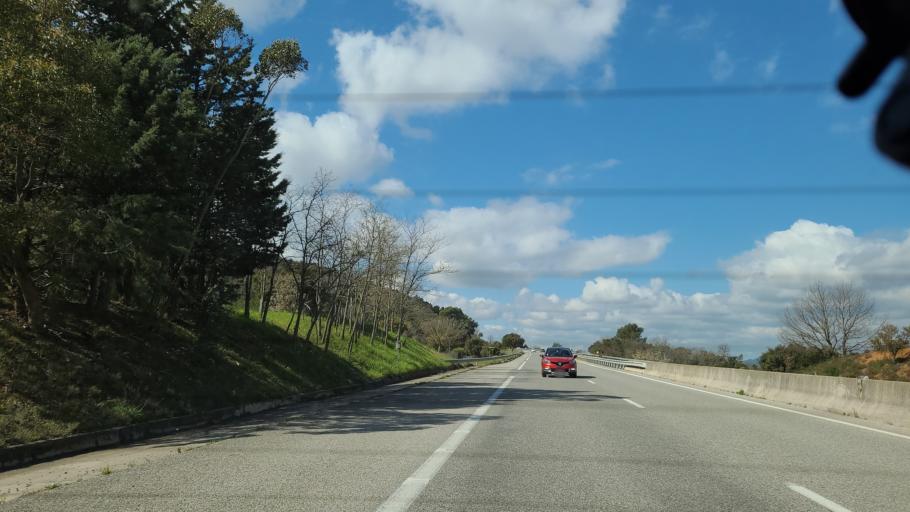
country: FR
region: Provence-Alpes-Cote d'Azur
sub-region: Departement du Var
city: Gonfaron
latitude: 43.3061
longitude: 6.2791
